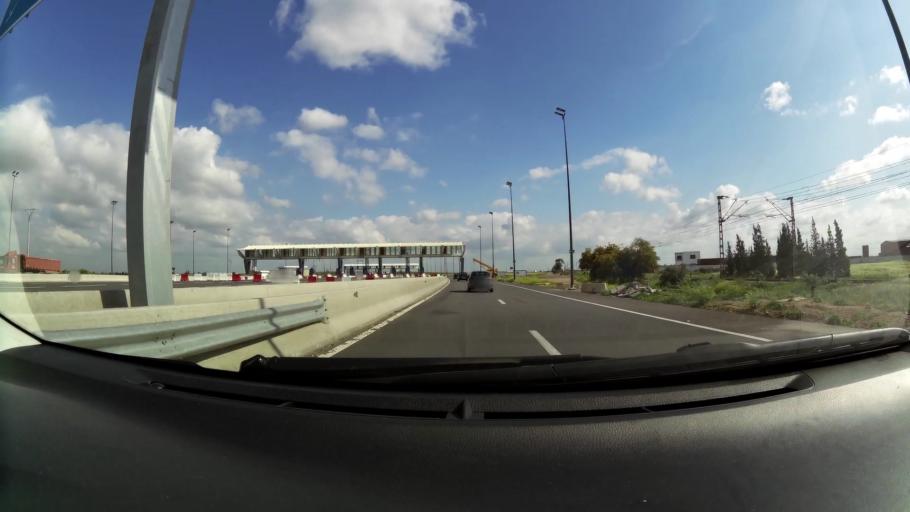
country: MA
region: Chaouia-Ouardigha
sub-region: Settat Province
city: Berrechid
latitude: 33.3214
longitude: -7.6052
